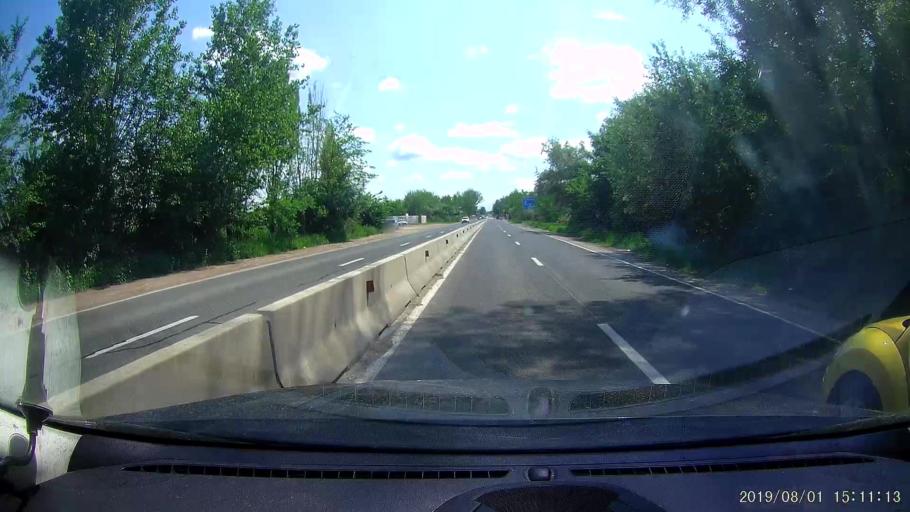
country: RO
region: Braila
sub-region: Comuna Chiscani
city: Chiscani
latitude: 45.2195
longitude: 27.9258
